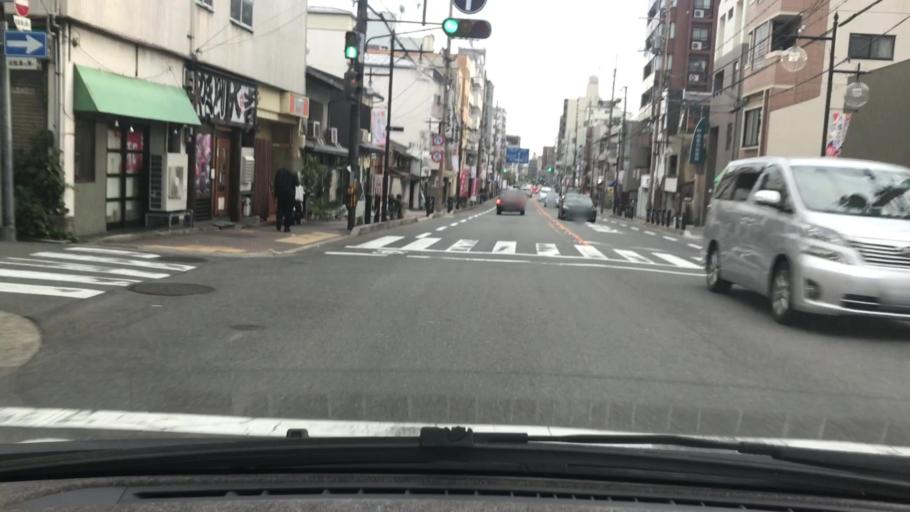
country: JP
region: Kyoto
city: Kyoto
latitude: 35.0201
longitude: 135.7427
